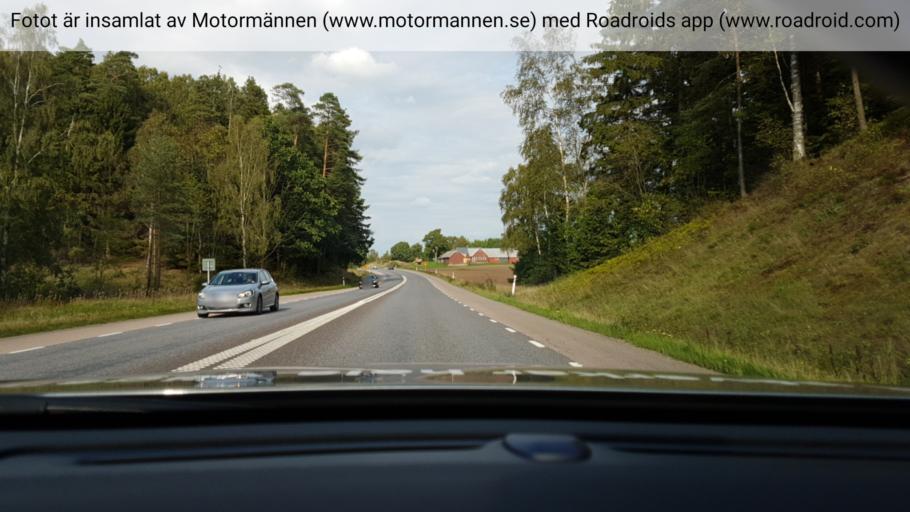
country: SE
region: Halland
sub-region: Halmstads Kommun
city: Aled
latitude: 56.7213
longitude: 12.9054
